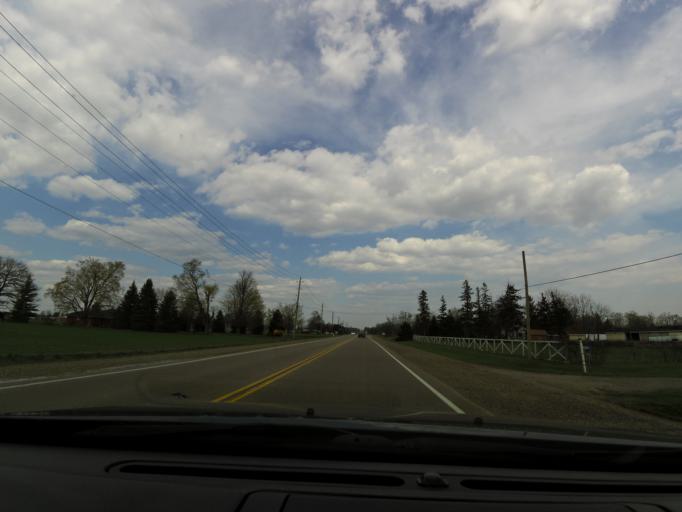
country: CA
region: Ontario
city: Ancaster
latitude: 43.2873
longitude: -80.0313
